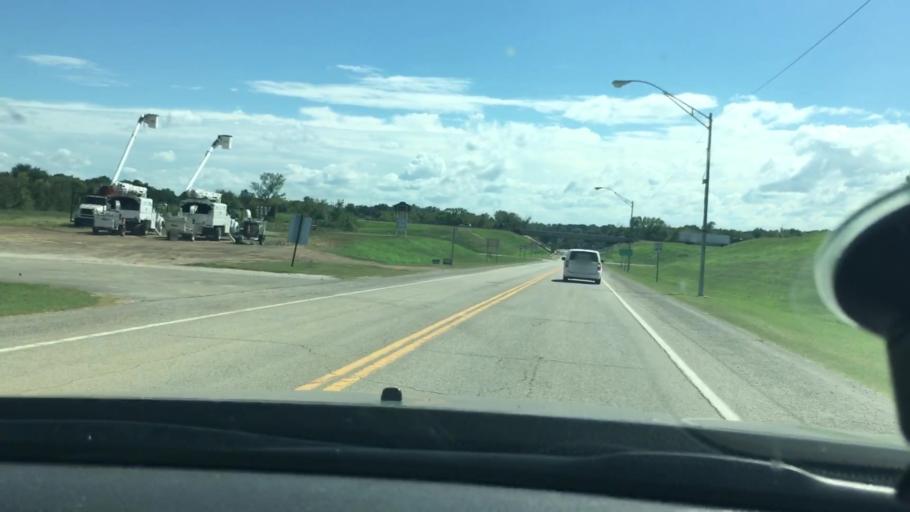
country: US
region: Oklahoma
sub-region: Sequoyah County
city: Vian
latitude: 35.4917
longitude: -94.9719
